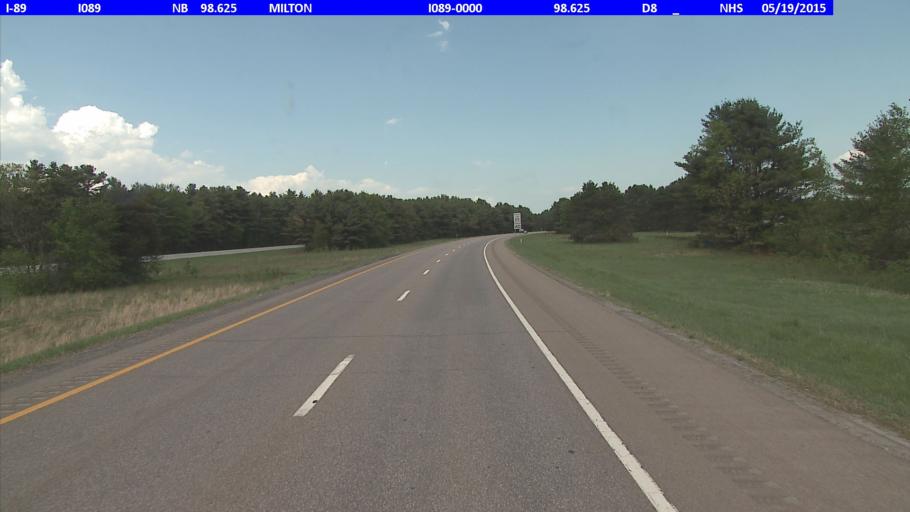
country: US
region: Vermont
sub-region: Chittenden County
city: Colchester
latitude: 44.6004
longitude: -73.1724
